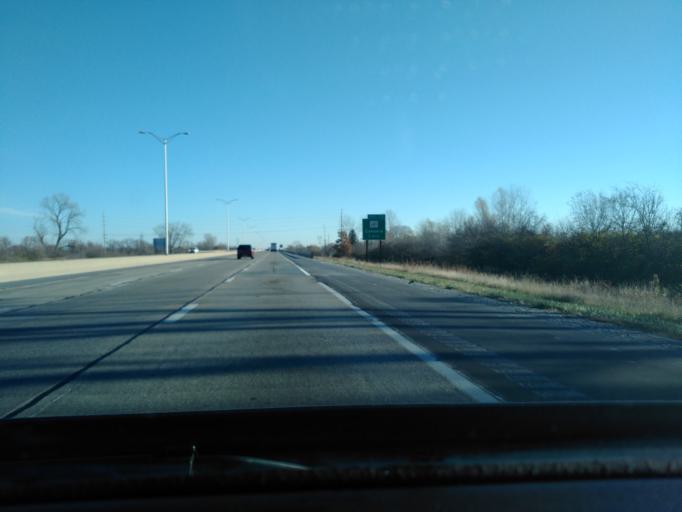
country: US
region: Illinois
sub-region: Saint Clair County
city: Cahokia
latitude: 38.5418
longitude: -90.1767
